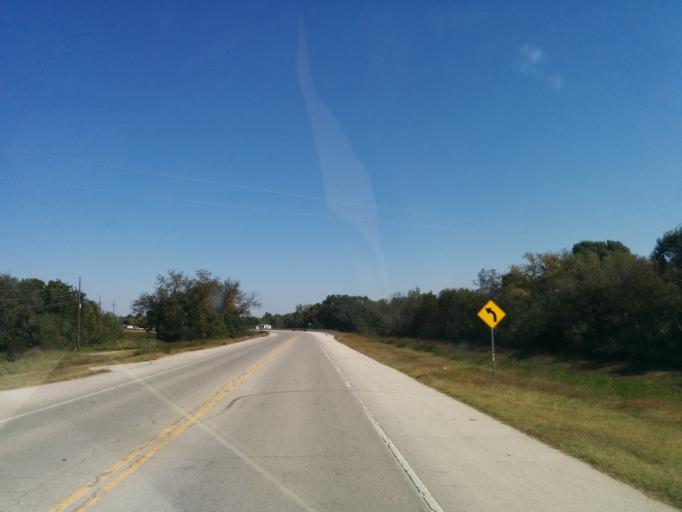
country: US
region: Oklahoma
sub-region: Creek County
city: Mounds
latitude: 35.8650
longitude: -96.0637
